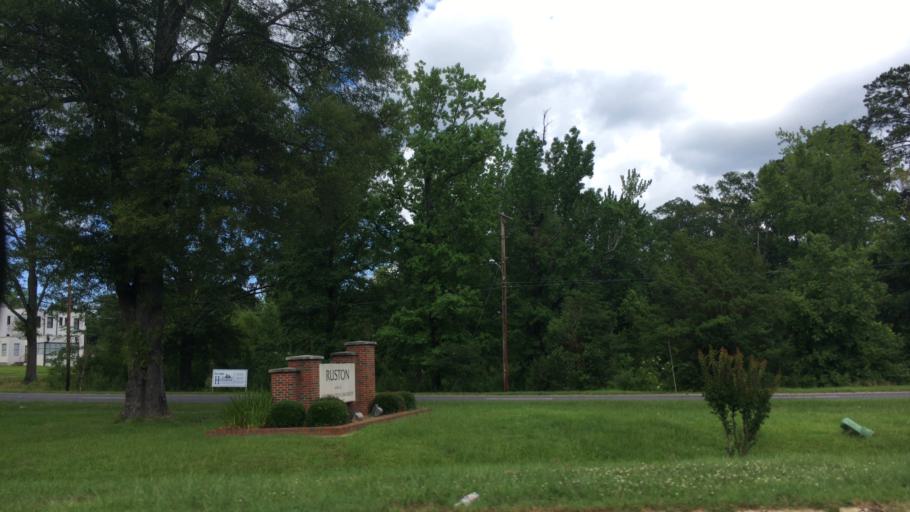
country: US
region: Louisiana
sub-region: Lincoln Parish
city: Ruston
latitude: 32.5202
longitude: -92.6391
